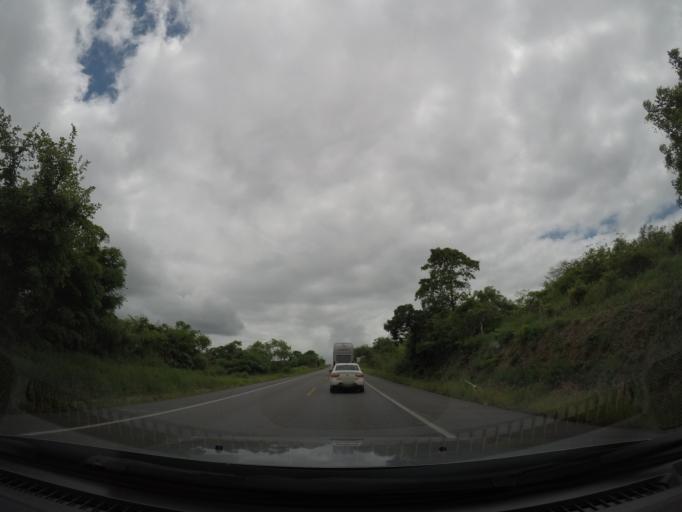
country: BR
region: Bahia
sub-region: Ruy Barbosa
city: Terra Nova
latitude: -12.4497
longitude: -40.6106
